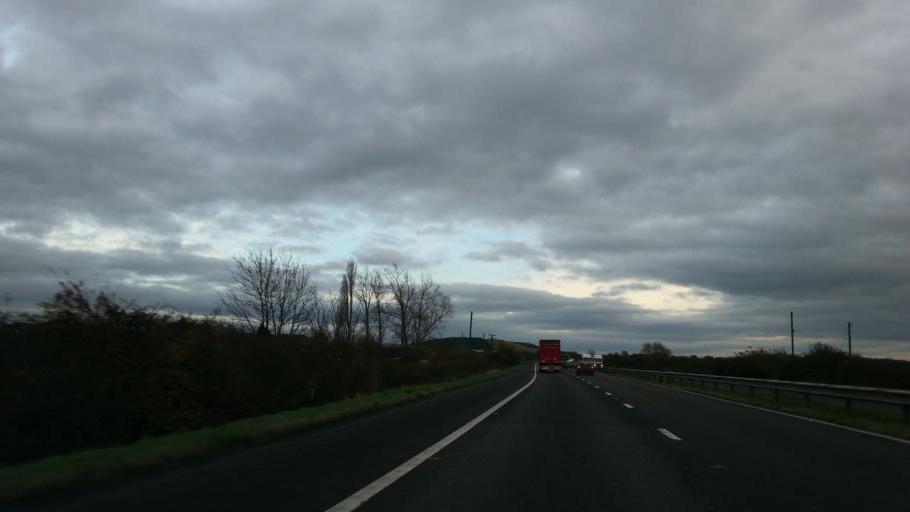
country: GB
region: England
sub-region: Doncaster
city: Tickhill
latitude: 53.4213
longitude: -1.0904
